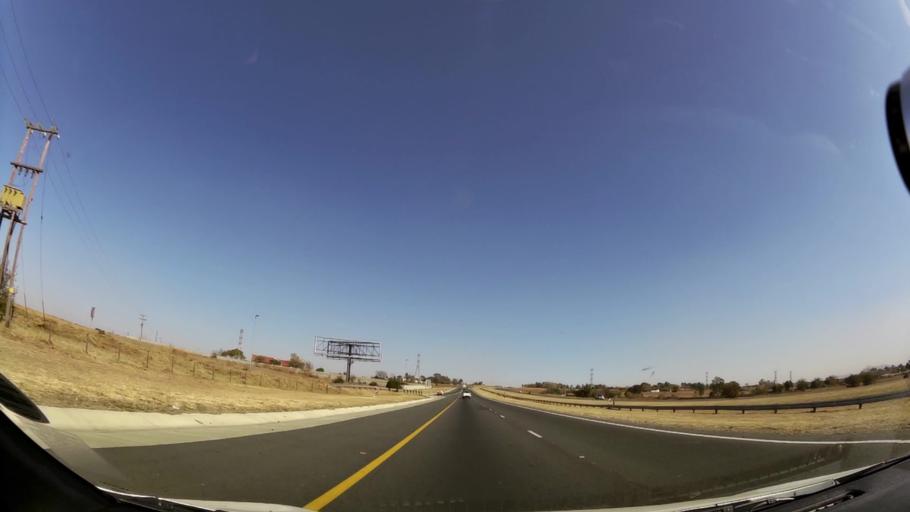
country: ZA
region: Gauteng
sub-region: City of Johannesburg Metropolitan Municipality
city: Diepsloot
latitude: -25.9618
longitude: 27.9503
